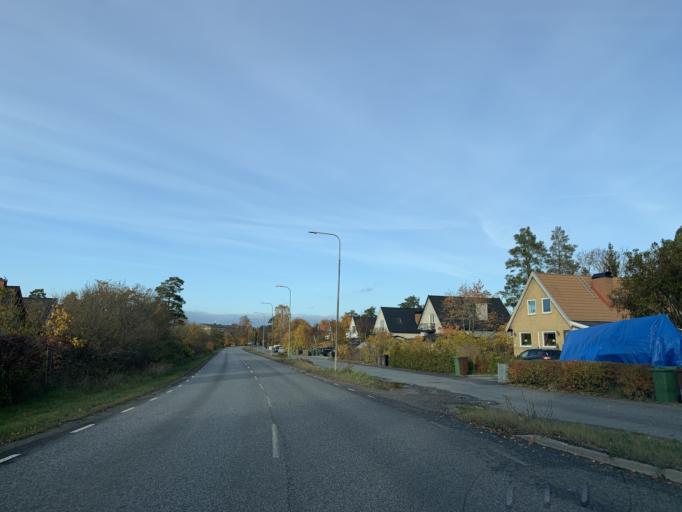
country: SE
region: Stockholm
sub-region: Haninge Kommun
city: Haninge
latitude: 59.1812
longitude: 18.1808
